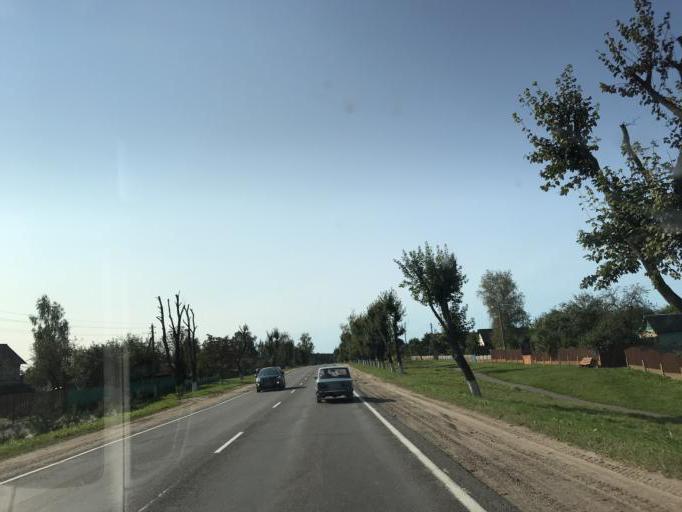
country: BY
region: Mogilev
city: Buynichy
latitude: 53.8272
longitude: 30.2423
